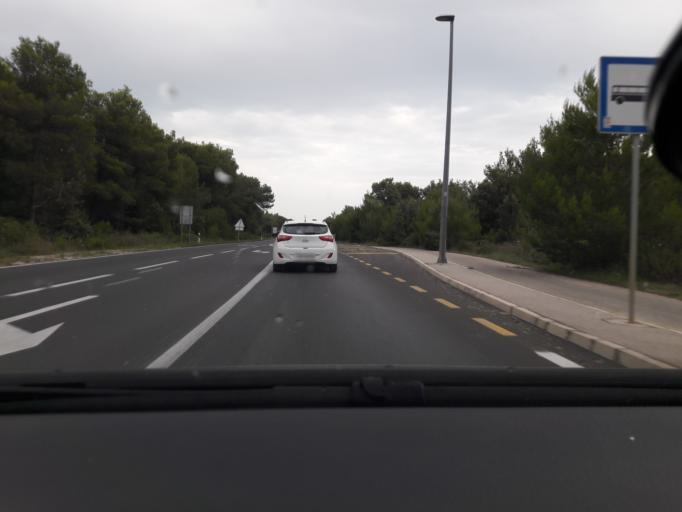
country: HR
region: Zadarska
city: Nin
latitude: 44.1927
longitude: 15.1790
